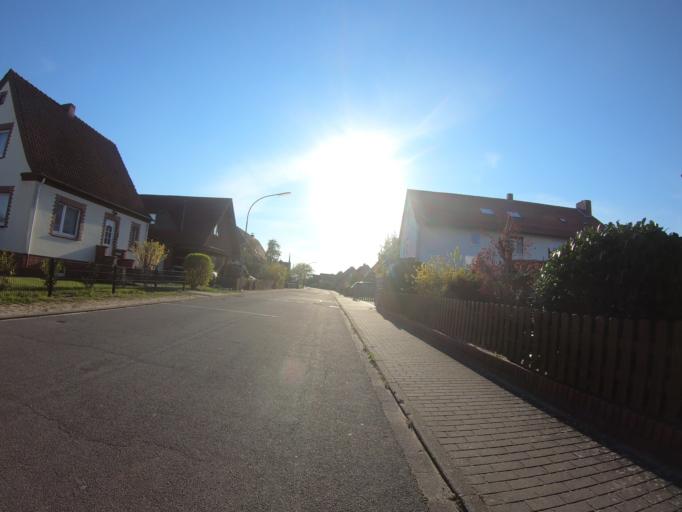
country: DE
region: Lower Saxony
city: Wagenhoff
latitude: 52.5181
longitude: 10.5351
